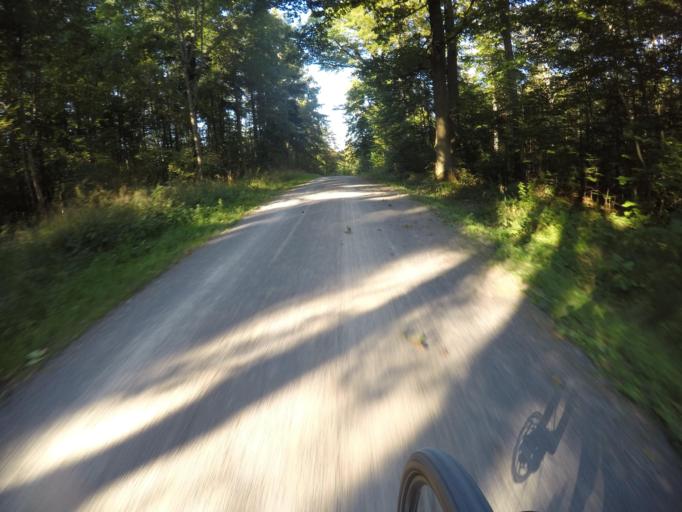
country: DE
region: Baden-Wuerttemberg
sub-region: Regierungsbezirk Stuttgart
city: Korntal
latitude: 48.7917
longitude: 9.1148
